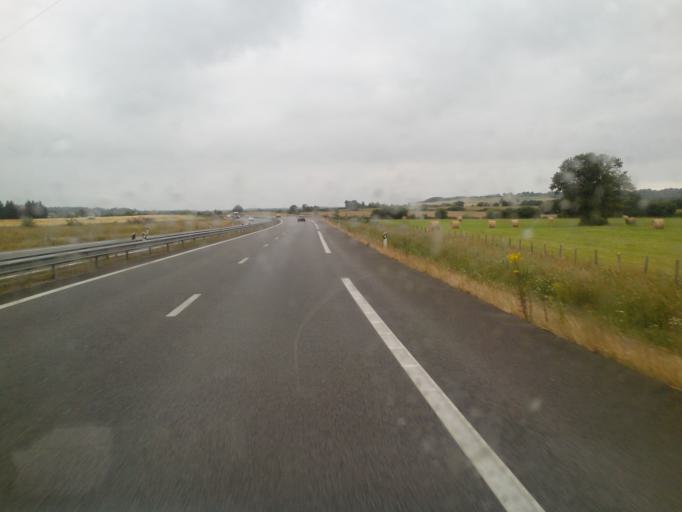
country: FR
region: Brittany
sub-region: Departement d'Ille-et-Vilaine
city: La Dominelais
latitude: 47.7744
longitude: -1.7033
